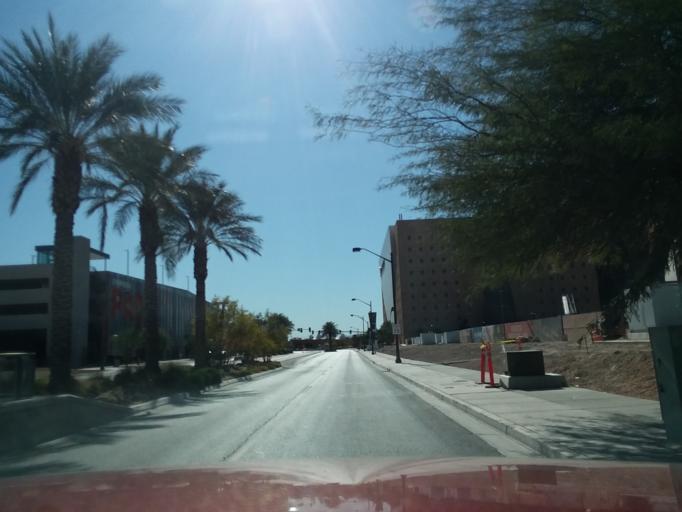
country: US
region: Nevada
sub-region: Clark County
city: Las Vegas
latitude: 36.1701
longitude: -115.1540
